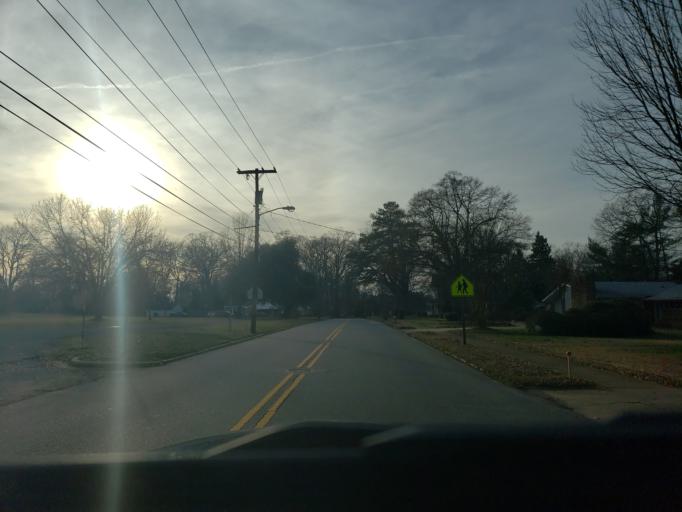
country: US
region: North Carolina
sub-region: Cleveland County
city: Shelby
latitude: 35.2899
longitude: -81.5587
